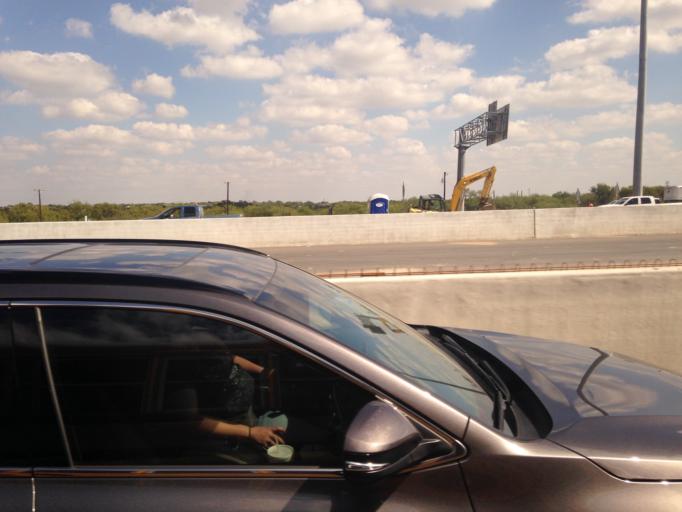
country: US
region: Texas
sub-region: Tarrant County
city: Blue Mound
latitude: 32.8798
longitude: -97.3175
